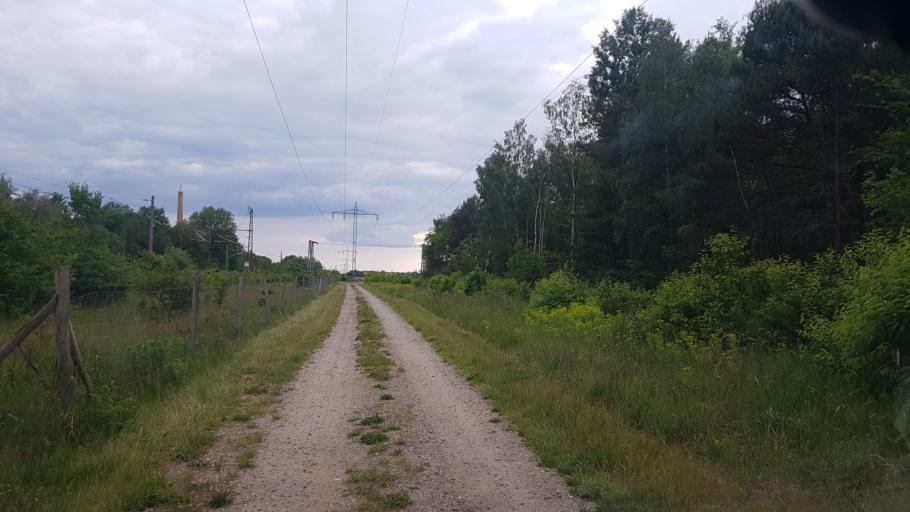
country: DE
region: Brandenburg
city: Trobitz
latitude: 51.6013
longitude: 13.4422
